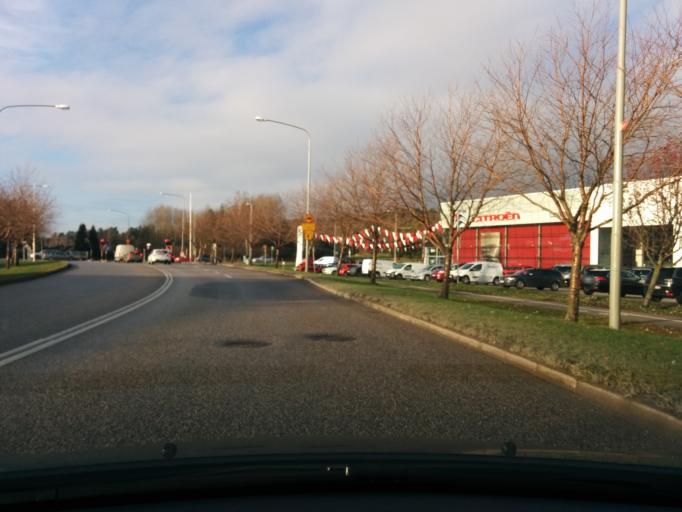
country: SE
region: Stockholm
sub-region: Jarfalla Kommun
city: Jakobsberg
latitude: 59.3914
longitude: 17.8715
